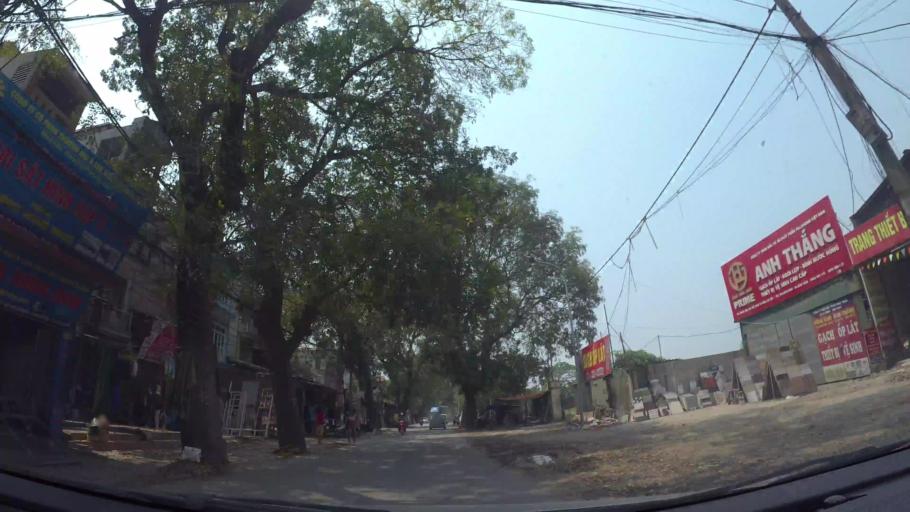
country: VN
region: Ha Noi
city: Ha Dong
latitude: 20.9866
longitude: 105.7675
